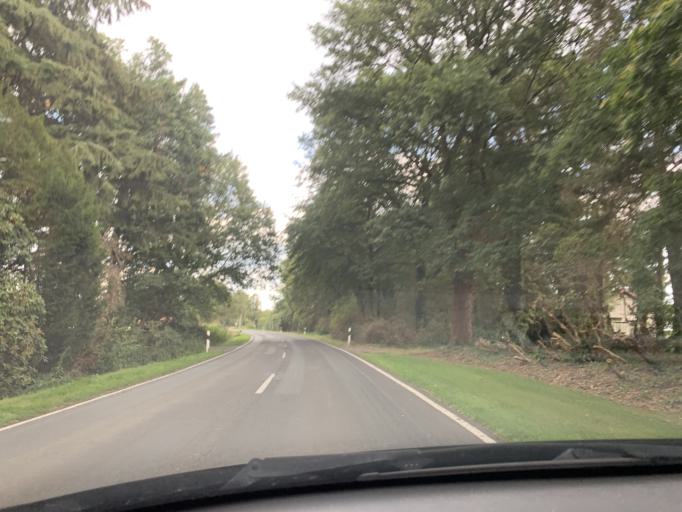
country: DE
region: Lower Saxony
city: Apen
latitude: 53.2227
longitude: 7.8427
